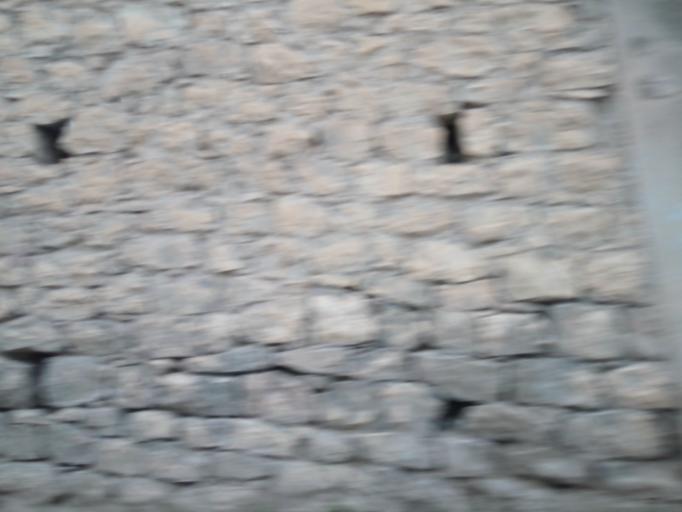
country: DZ
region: Constantine
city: Constantine
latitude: 36.3709
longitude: 6.6197
